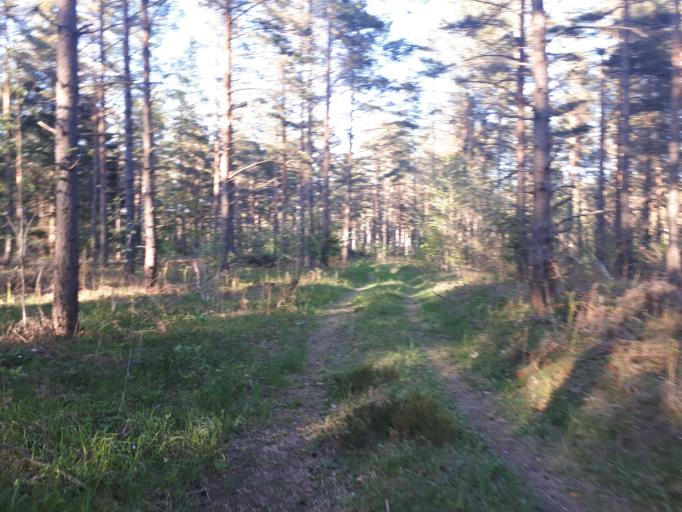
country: SE
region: Gotland
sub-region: Gotland
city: Visby
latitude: 57.6017
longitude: 18.2901
